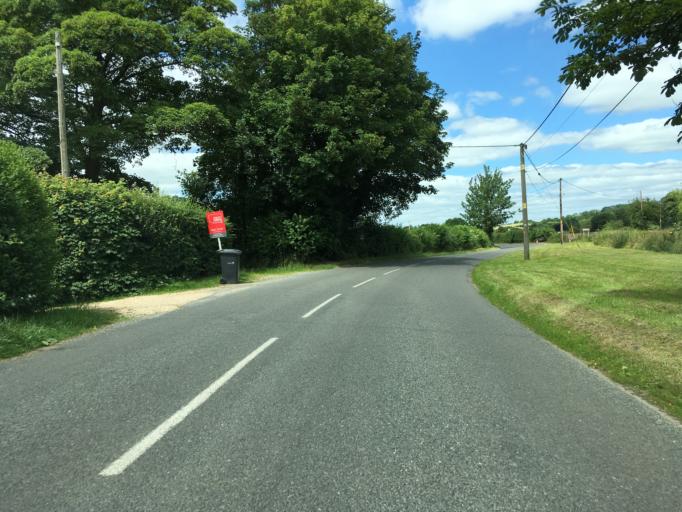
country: GB
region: England
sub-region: Hampshire
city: Highclere
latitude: 51.2598
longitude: -1.4161
